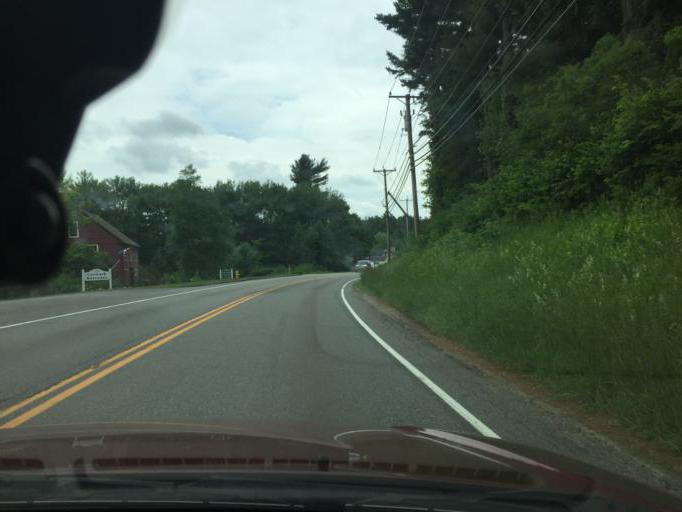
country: US
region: Connecticut
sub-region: Litchfield County
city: Litchfield
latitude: 41.7340
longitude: -73.2156
